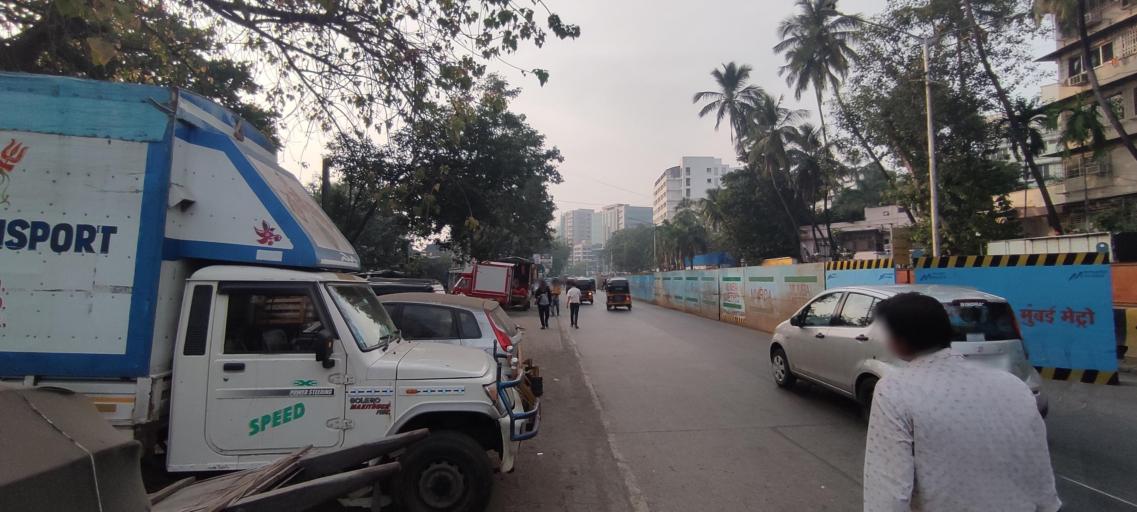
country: IN
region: Maharashtra
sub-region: Mumbai Suburban
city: Mumbai
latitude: 19.1015
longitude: 72.8390
